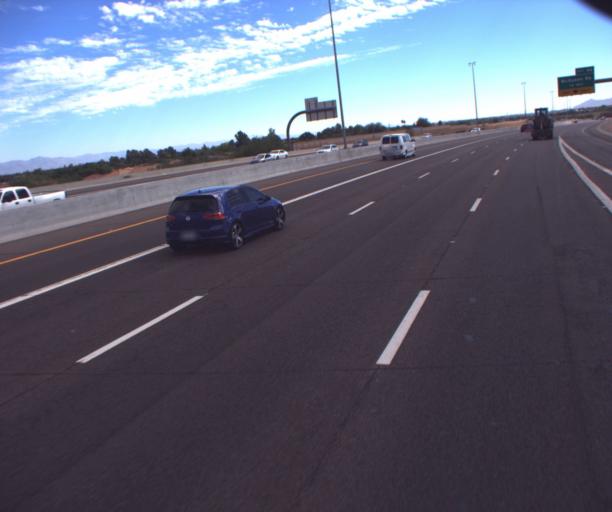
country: US
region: Arizona
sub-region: Maricopa County
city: Chandler
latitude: 33.2861
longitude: -111.8353
